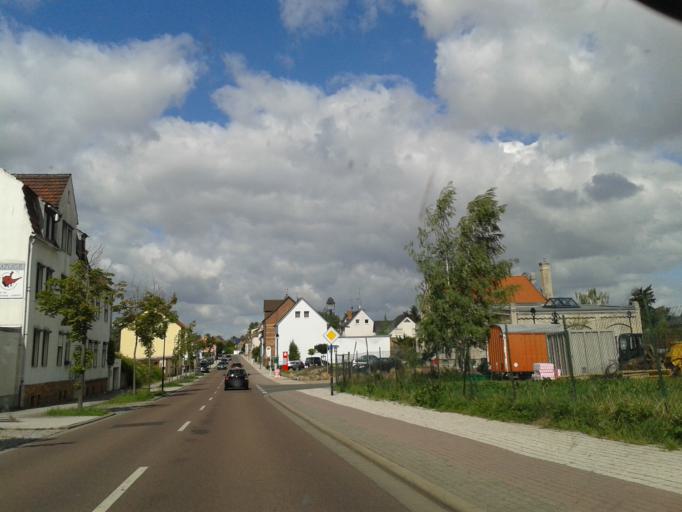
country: DE
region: Saxony-Anhalt
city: Lieskau
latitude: 51.5115
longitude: 11.8932
